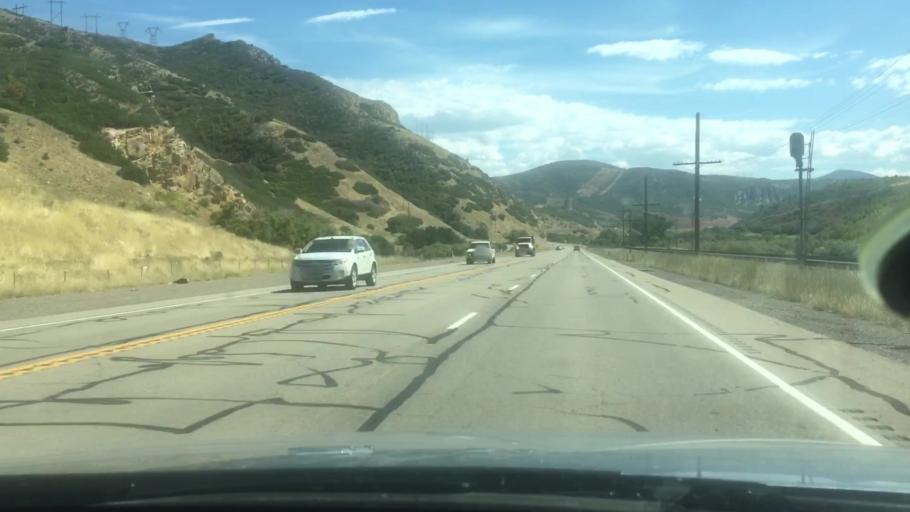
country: US
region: Utah
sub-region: Utah County
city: Mapleton
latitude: 40.0374
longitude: -111.5325
